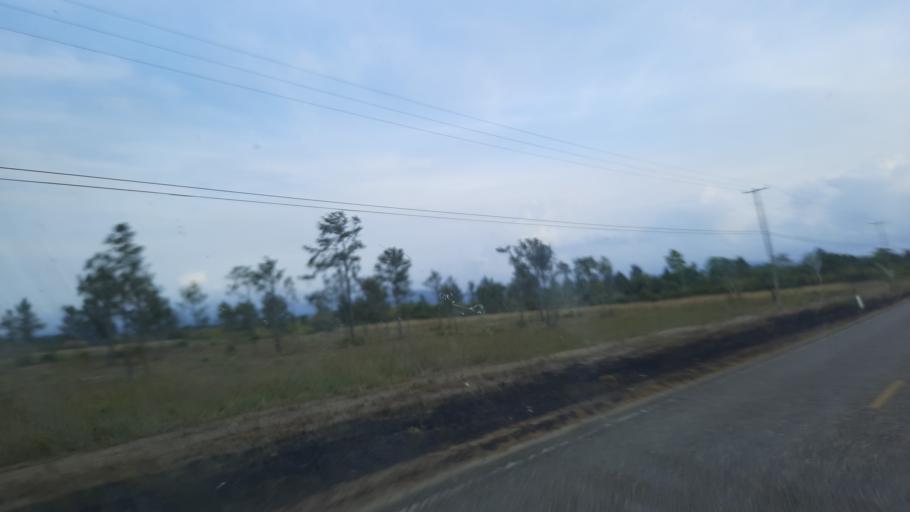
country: BZ
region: Stann Creek
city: Placencia
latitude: 16.5690
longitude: -88.5152
